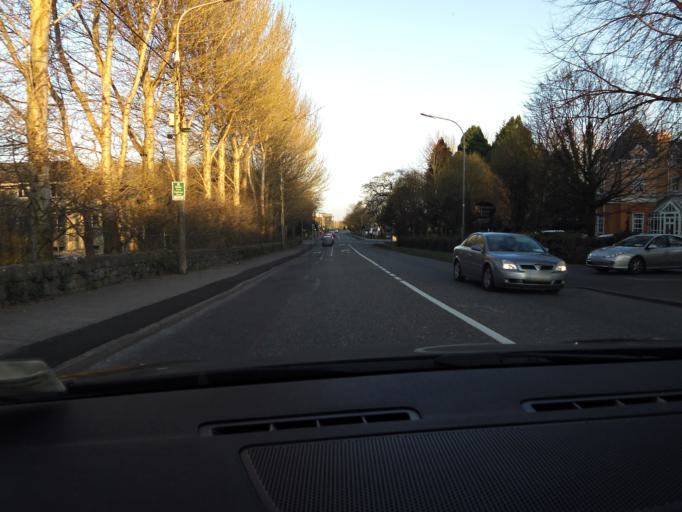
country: IE
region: Connaught
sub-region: County Galway
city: Gaillimh
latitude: 53.2898
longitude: -9.0753
